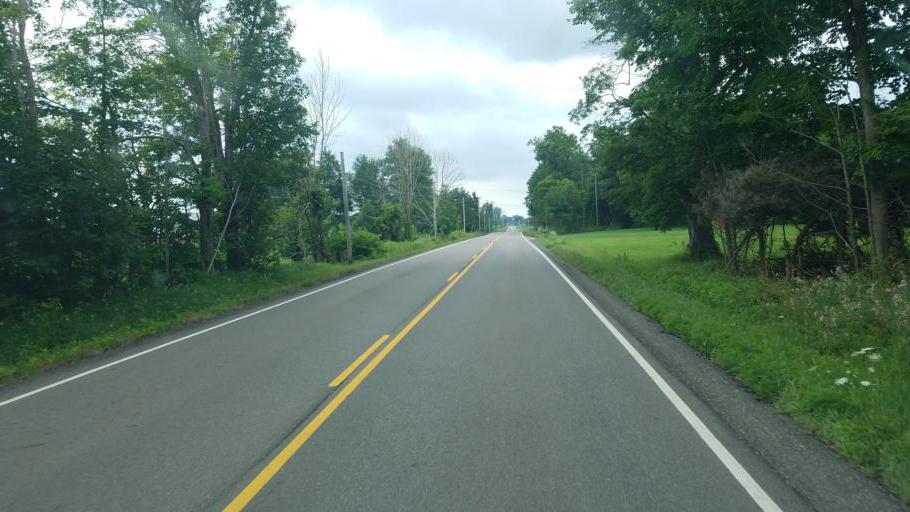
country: US
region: Ohio
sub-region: Licking County
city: Utica
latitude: 40.2766
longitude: -82.5154
